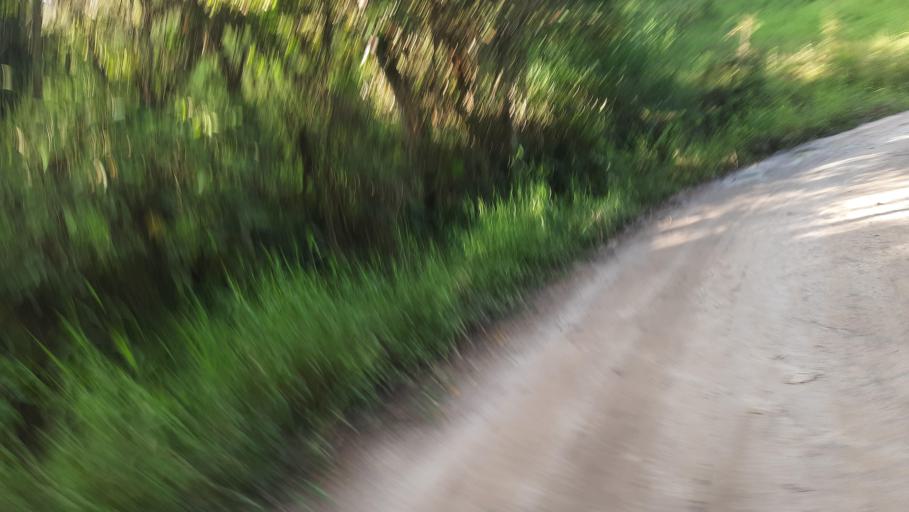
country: CO
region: Cundinamarca
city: Tenza
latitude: 5.1022
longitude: -73.4354
